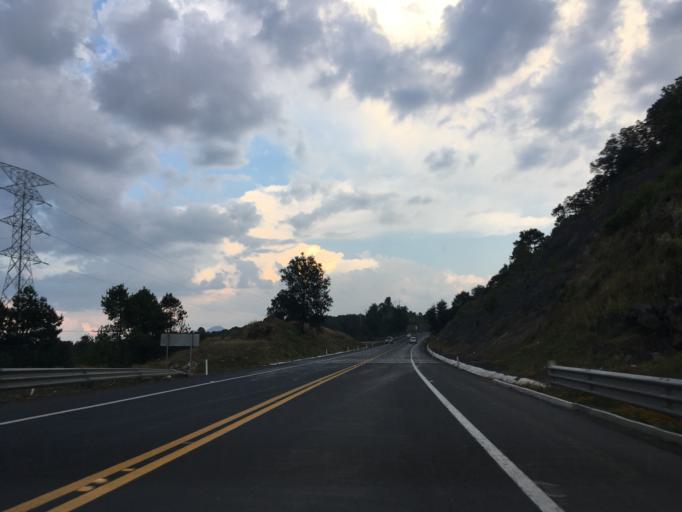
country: MX
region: Michoacan
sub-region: Patzcuaro
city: Santa Ana Chapitiro
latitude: 19.5013
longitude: -101.6379
